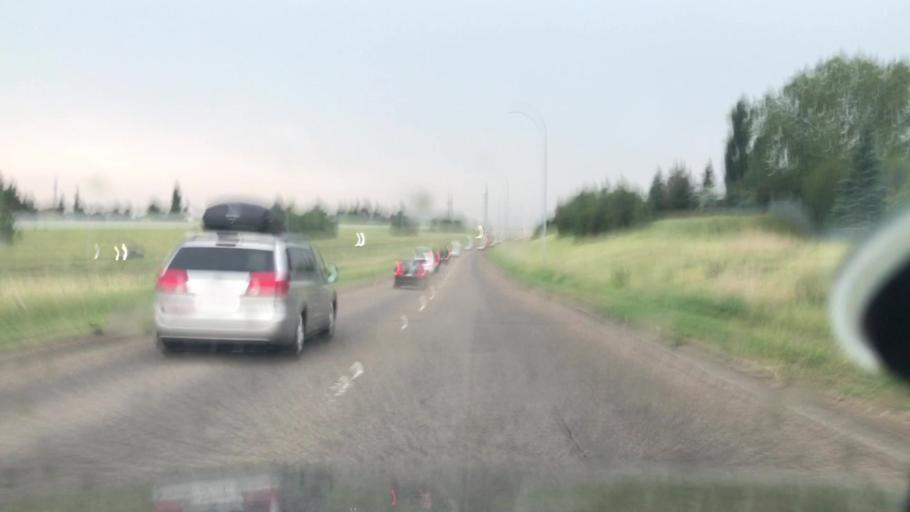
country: CA
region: Alberta
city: Edmonton
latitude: 53.4678
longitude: -113.5833
